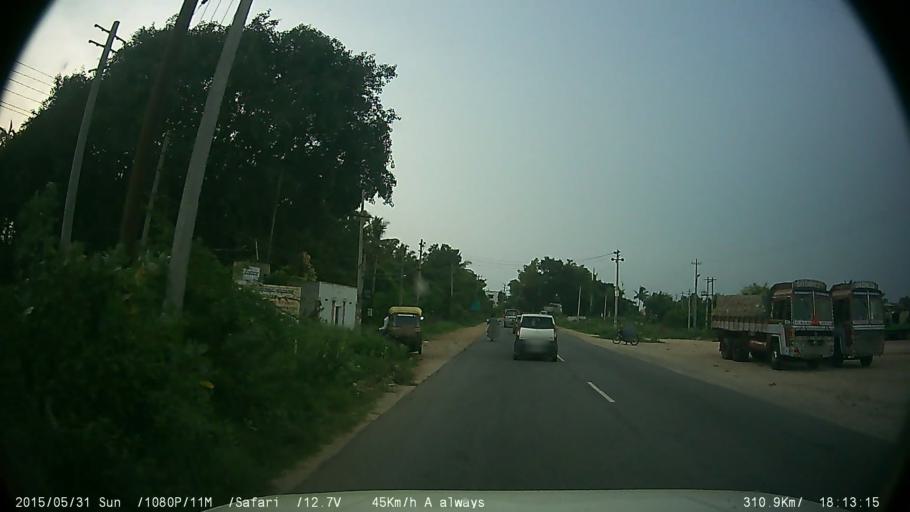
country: IN
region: Karnataka
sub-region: Mysore
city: Nanjangud
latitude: 12.1014
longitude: 76.6716
